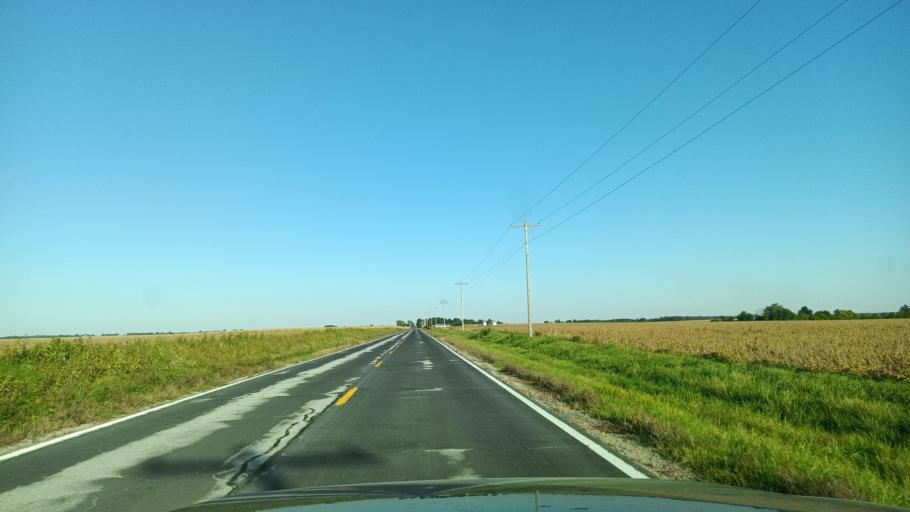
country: US
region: Illinois
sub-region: Mercer County
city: Aledo
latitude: 41.0679
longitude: -90.7010
